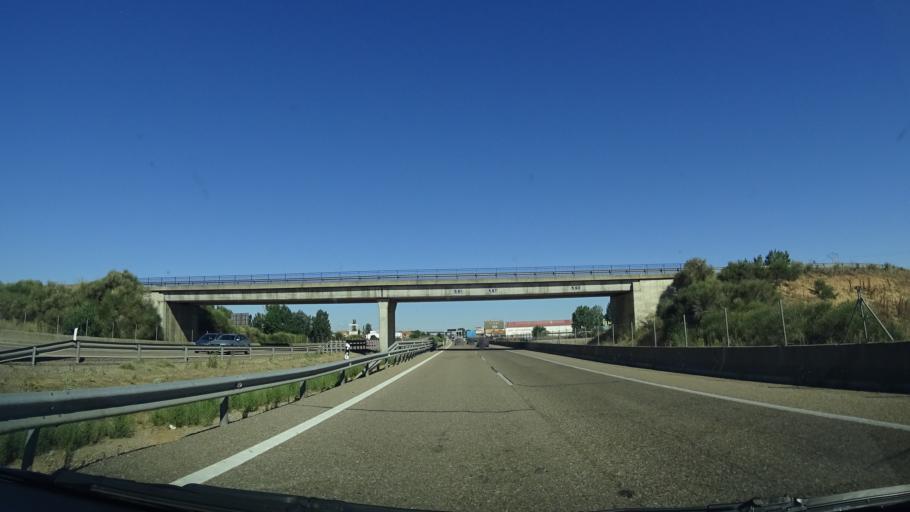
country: ES
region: Castille and Leon
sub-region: Provincia de Zamora
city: San Esteban del Molar
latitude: 41.9371
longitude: -5.5449
